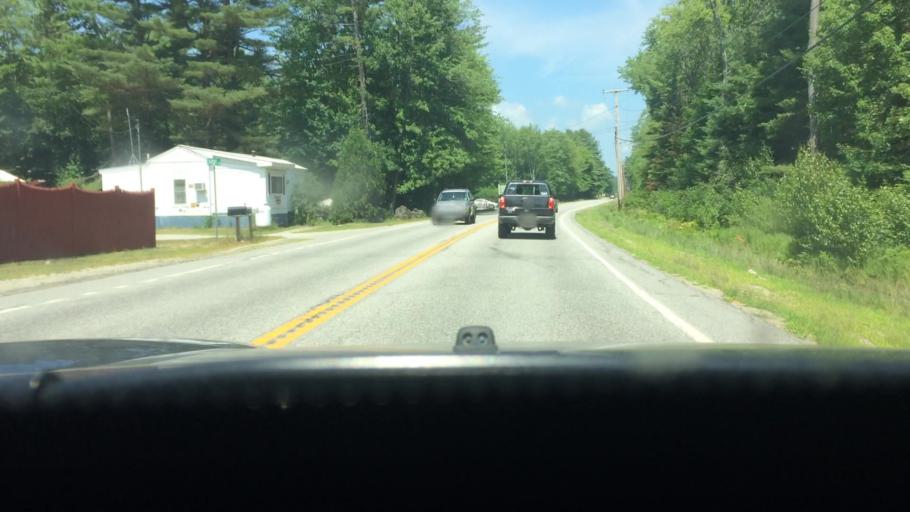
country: US
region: Maine
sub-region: Androscoggin County
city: Mechanic Falls
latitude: 44.0964
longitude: -70.3577
